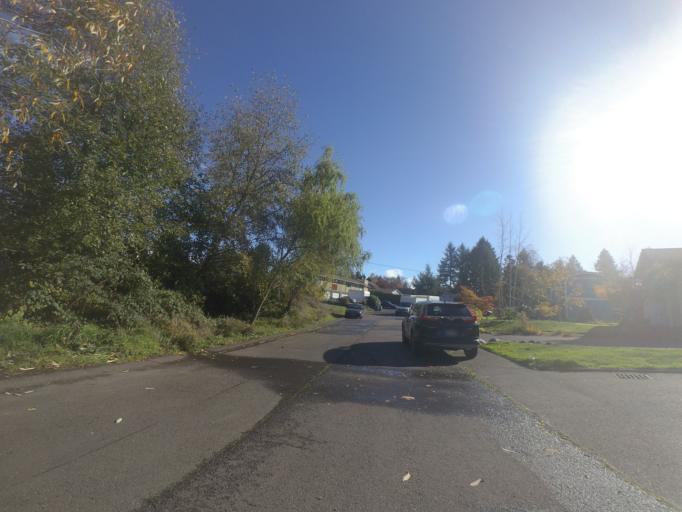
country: US
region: Washington
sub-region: Pierce County
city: University Place
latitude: 47.2338
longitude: -122.5554
